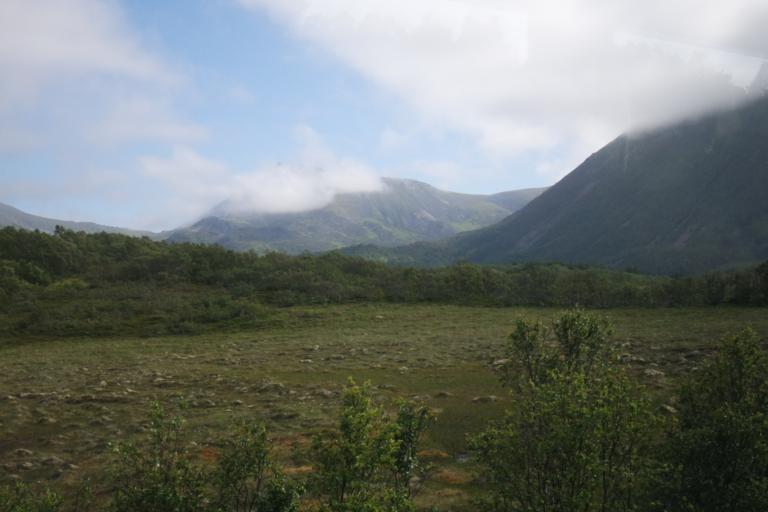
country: NO
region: Nordland
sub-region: Sortland
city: Sortland
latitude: 69.0096
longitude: 15.5573
